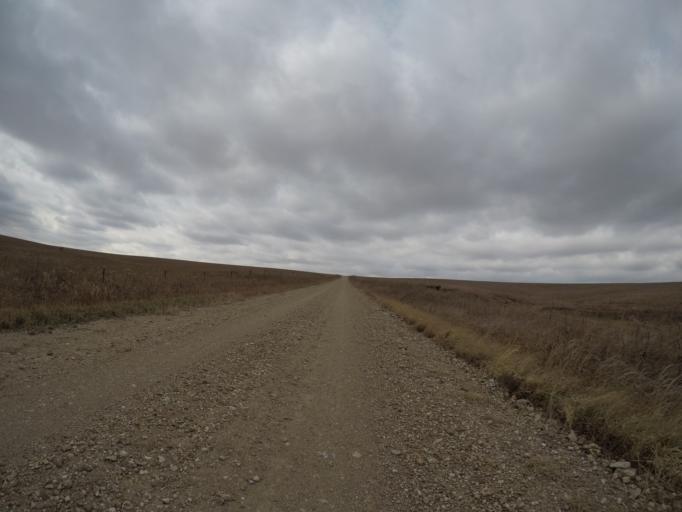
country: US
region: Kansas
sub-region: Morris County
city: Council Grove
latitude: 38.7244
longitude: -96.2028
